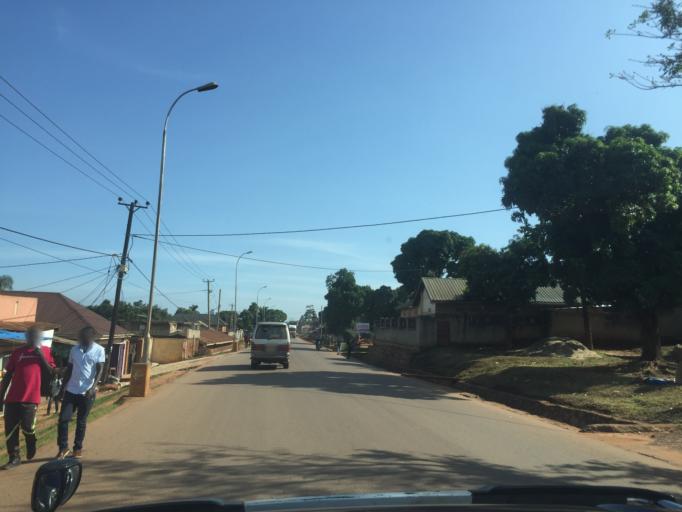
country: UG
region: Central Region
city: Kampala Central Division
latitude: 0.3693
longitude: 32.5692
